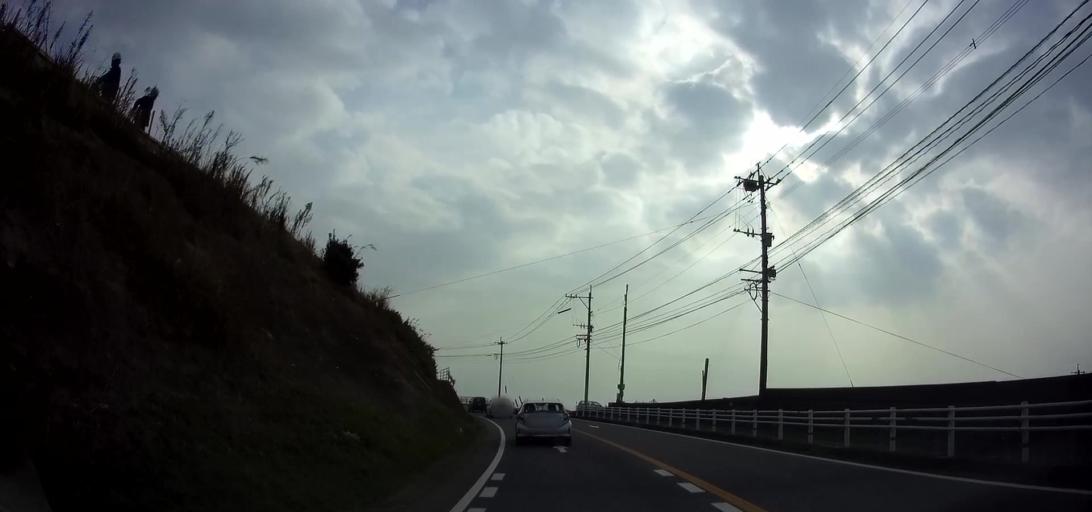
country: JP
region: Nagasaki
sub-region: Isahaya-shi
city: Isahaya
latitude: 32.7903
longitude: 130.0664
